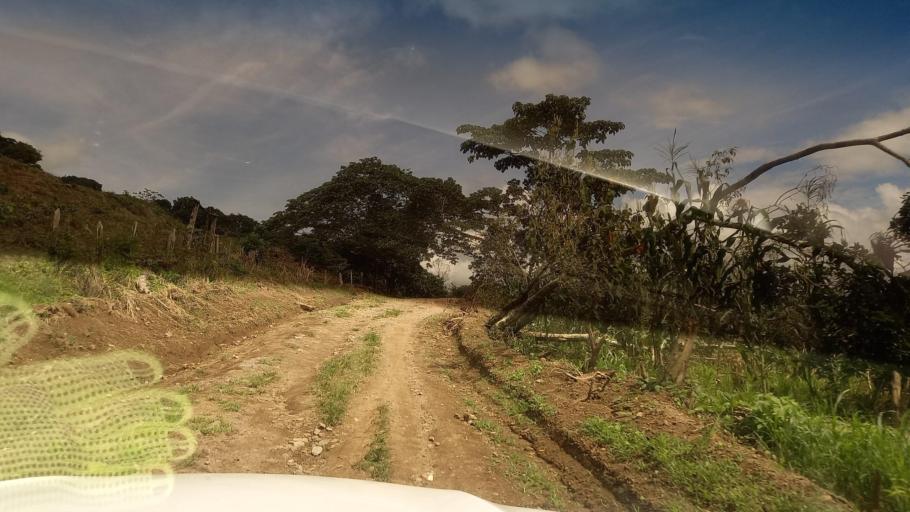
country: NI
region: Jinotega
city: San Jose de Bocay
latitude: 13.4013
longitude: -85.7005
